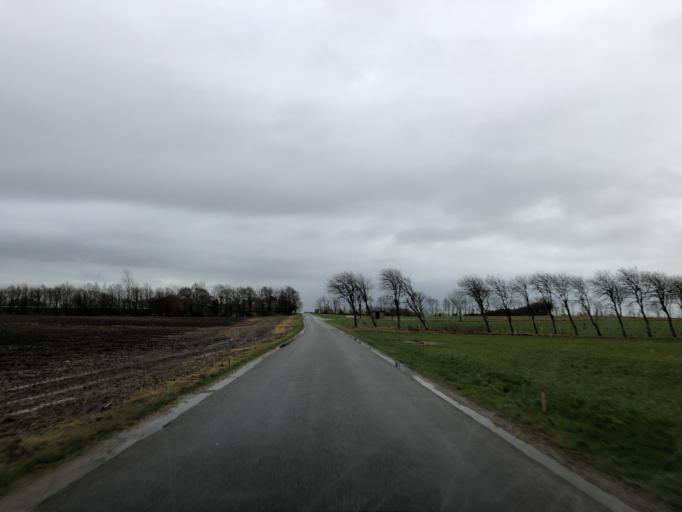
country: DK
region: Central Jutland
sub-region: Holstebro Kommune
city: Holstebro
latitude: 56.3791
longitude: 8.7274
